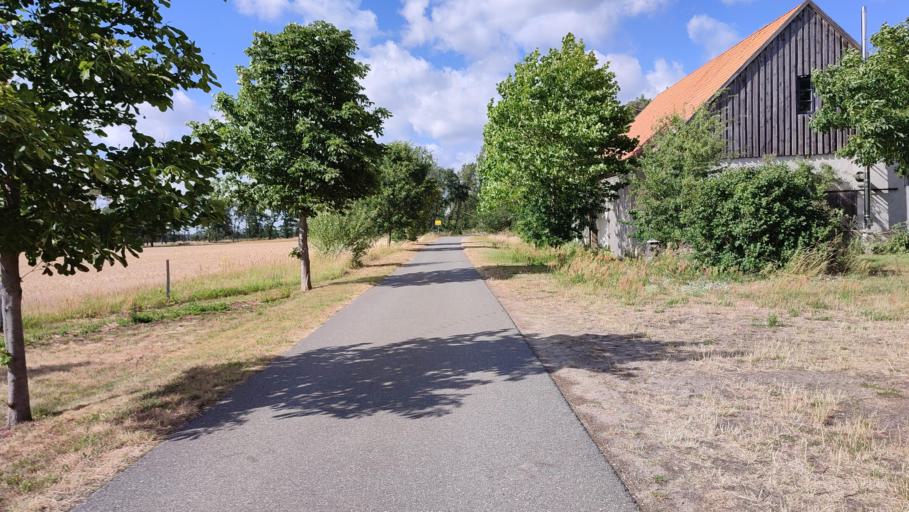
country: DE
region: Lower Saxony
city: Damnatz
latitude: 53.1743
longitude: 11.1689
